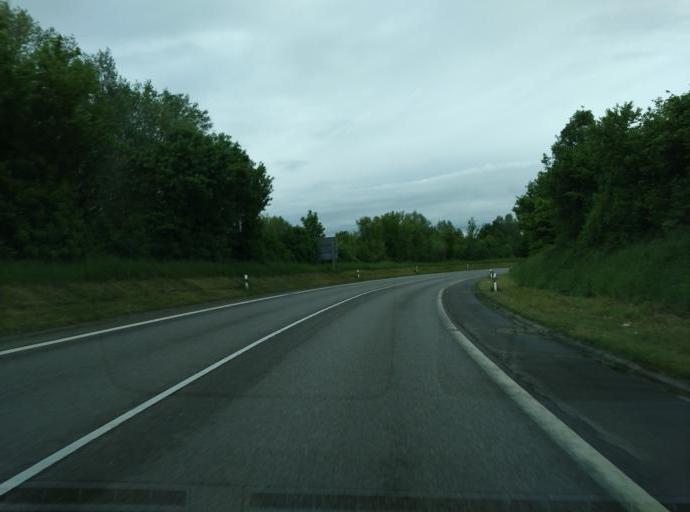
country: DE
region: Baden-Wuerttemberg
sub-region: Regierungsbezirk Stuttgart
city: Neckartailfingen
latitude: 48.6155
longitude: 9.2782
